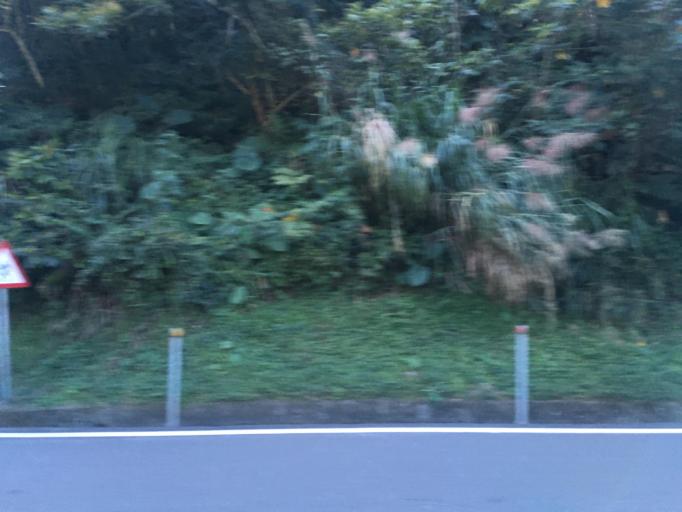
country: TW
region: Taiwan
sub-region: Chiayi
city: Jiayi Shi
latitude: 23.4168
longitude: 120.6438
